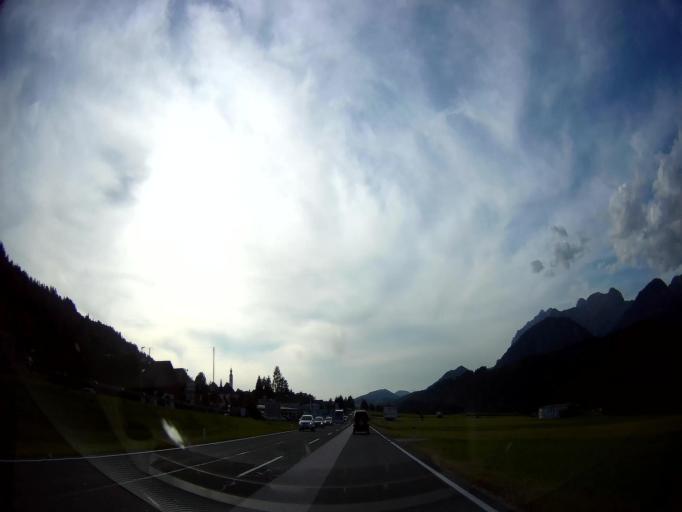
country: AT
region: Styria
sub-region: Politischer Bezirk Liezen
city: Haus im Ennstal
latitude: 47.4126
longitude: 13.7756
